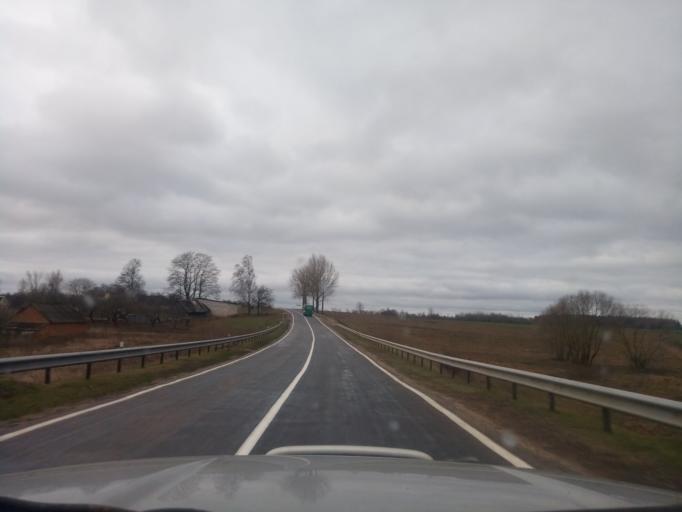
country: BY
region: Minsk
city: Kapyl'
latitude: 53.1785
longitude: 27.1680
